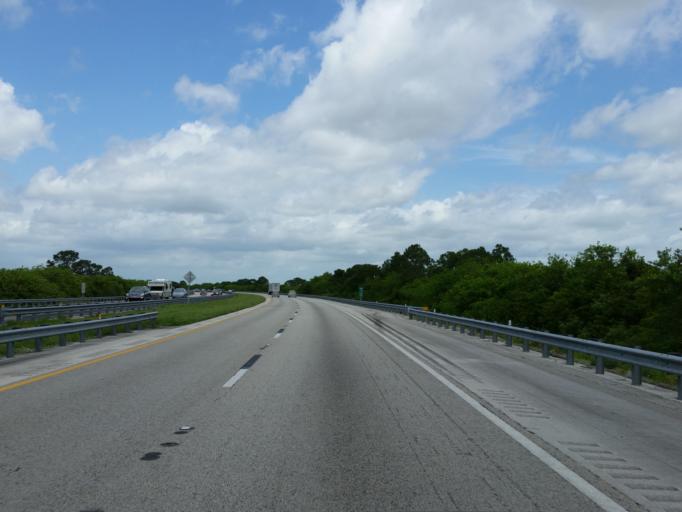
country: US
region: Florida
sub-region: Saint Lucie County
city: Lakewood Park
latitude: 27.4806
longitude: -80.4538
